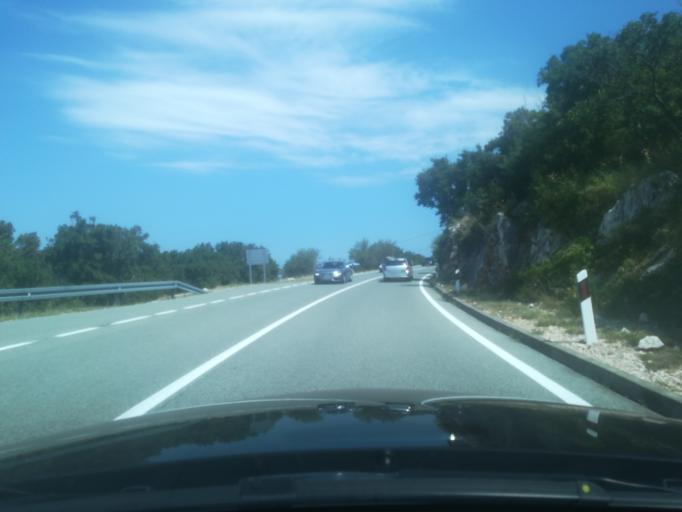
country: HR
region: Primorsko-Goranska
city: Banjol
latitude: 44.8057
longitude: 14.8976
